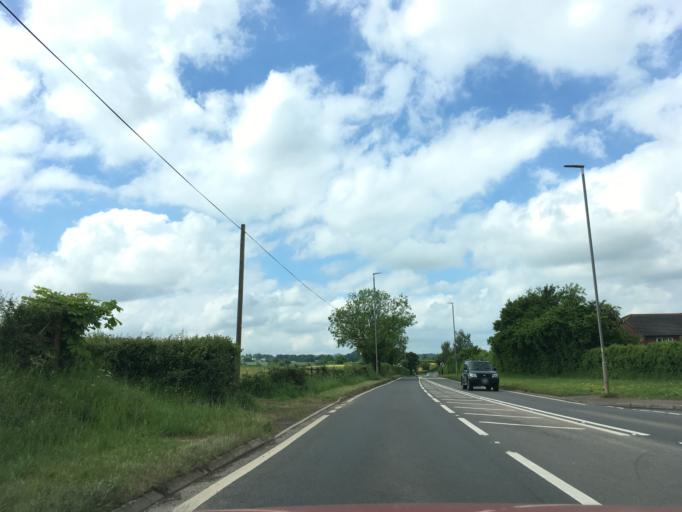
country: GB
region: England
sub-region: Somerset
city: Bishops Lydeard
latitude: 50.9683
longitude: -3.2294
